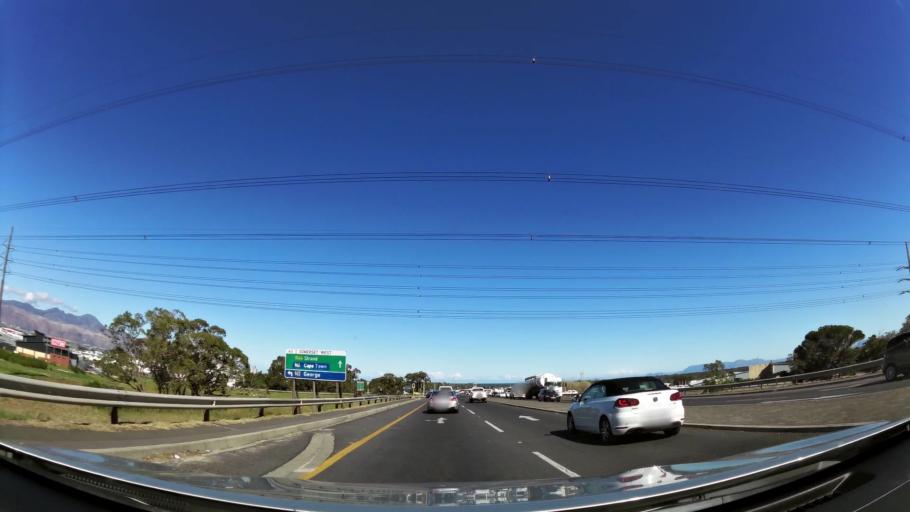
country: ZA
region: Western Cape
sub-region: Cape Winelands District Municipality
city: Stellenbosch
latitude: -34.0756
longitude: 18.8219
